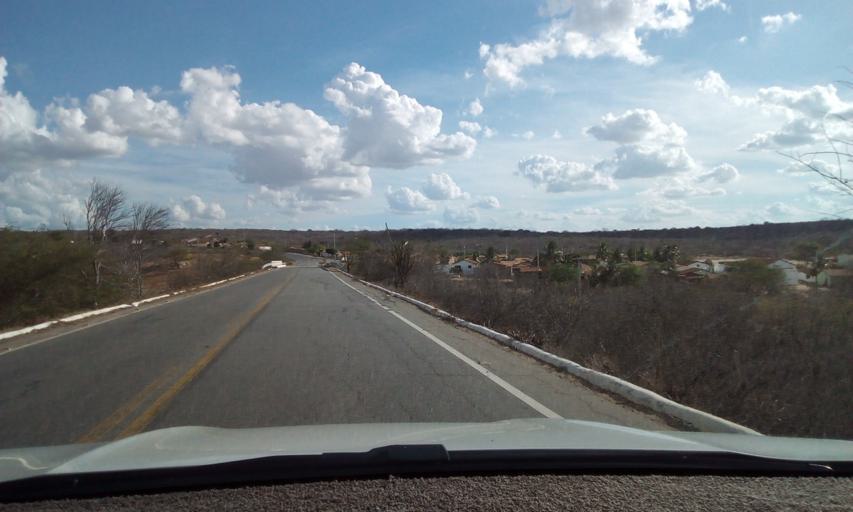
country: BR
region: Paraiba
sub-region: Soledade
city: Soledade
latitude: -6.8549
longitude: -36.4081
